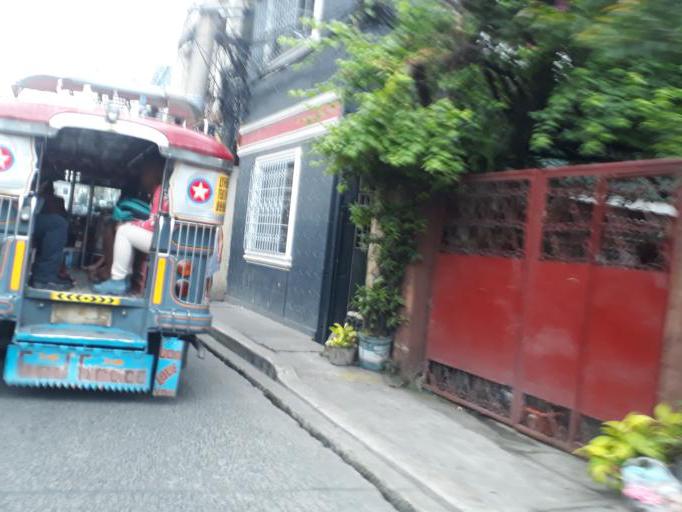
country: PH
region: Calabarzon
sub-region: Province of Rizal
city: Navotas
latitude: 14.6564
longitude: 120.9466
